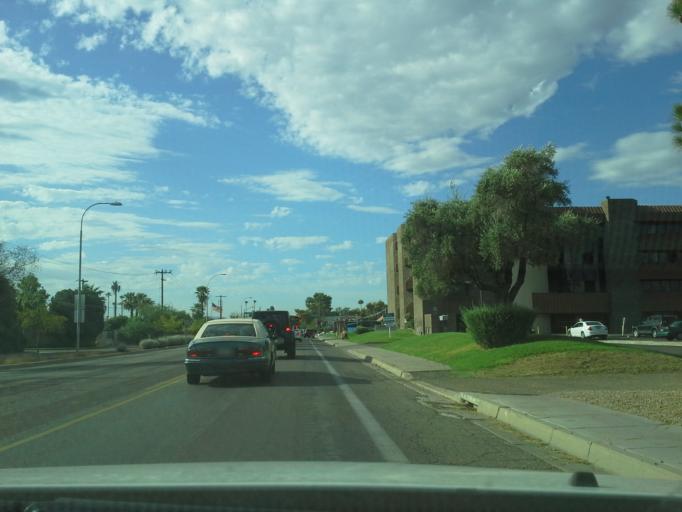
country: US
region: Arizona
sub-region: Maricopa County
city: Phoenix
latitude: 33.5115
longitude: -112.0913
